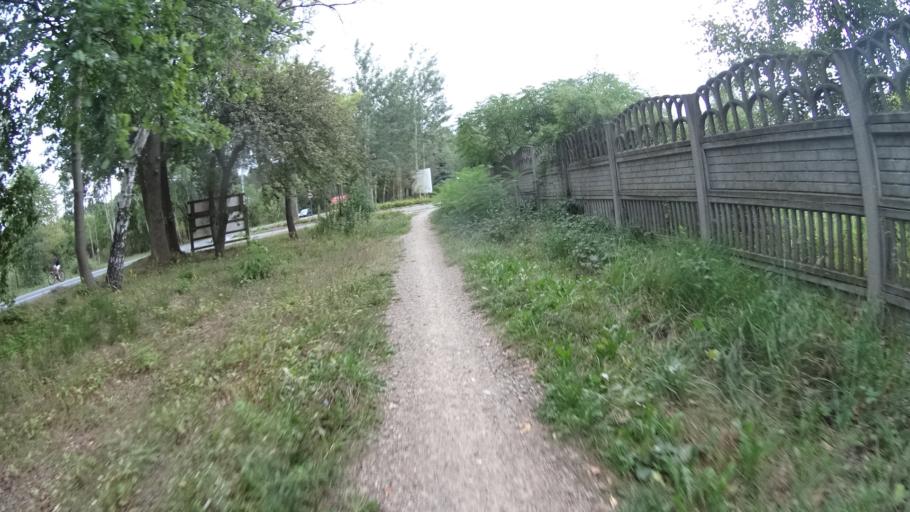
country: PL
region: Masovian Voivodeship
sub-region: Powiat pruszkowski
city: Granica
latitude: 52.1253
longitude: 20.7986
